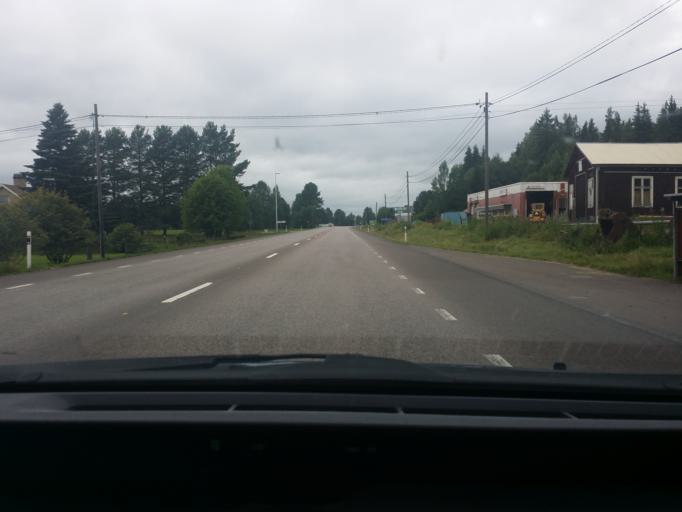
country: SE
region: Dalarna
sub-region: Gagnefs Kommun
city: Djuras
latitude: 60.5557
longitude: 15.1475
